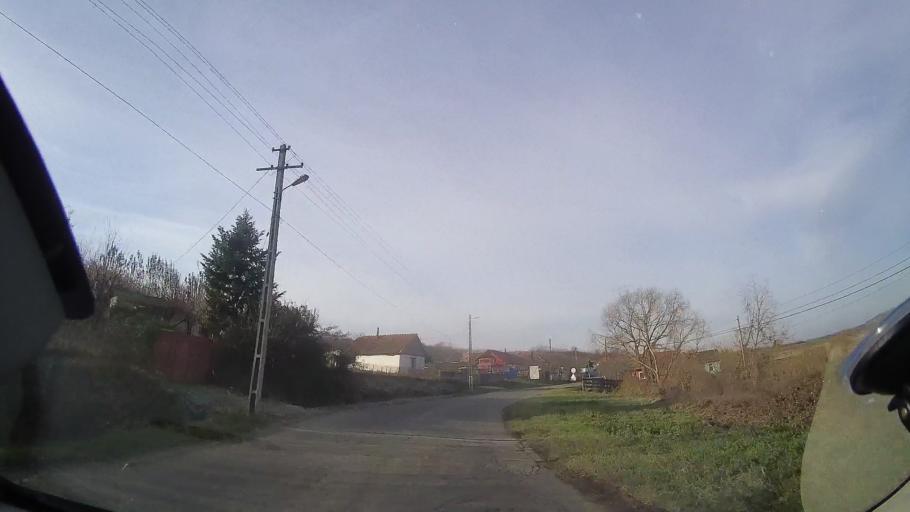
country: RO
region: Bihor
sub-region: Comuna Spinus
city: Spinus
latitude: 47.1806
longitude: 22.2128
